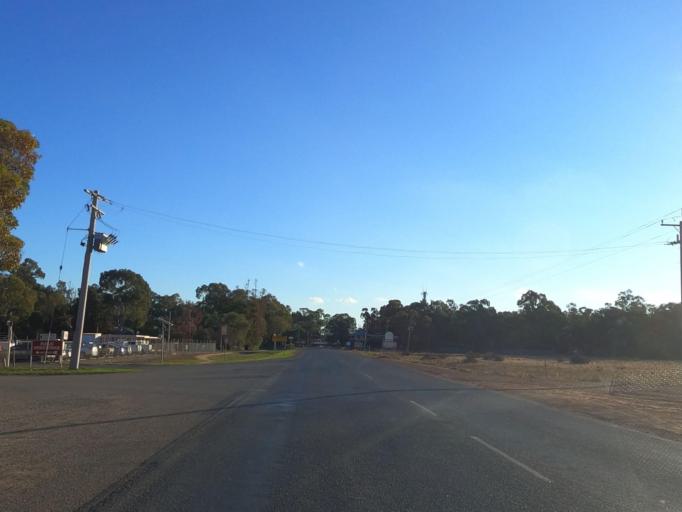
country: AU
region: Victoria
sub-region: Swan Hill
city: Swan Hill
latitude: -35.3372
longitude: 143.5679
